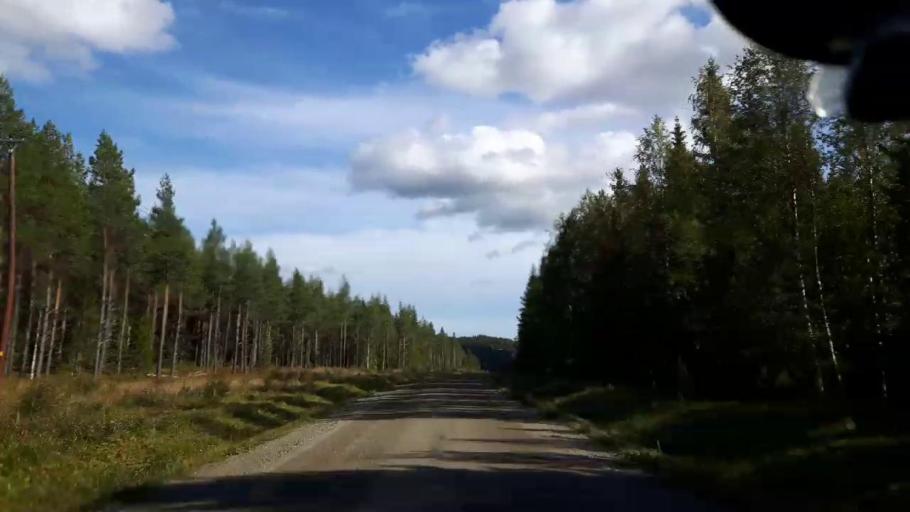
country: SE
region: Jaemtland
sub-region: Ragunda Kommun
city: Hammarstrand
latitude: 63.4289
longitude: 16.0504
